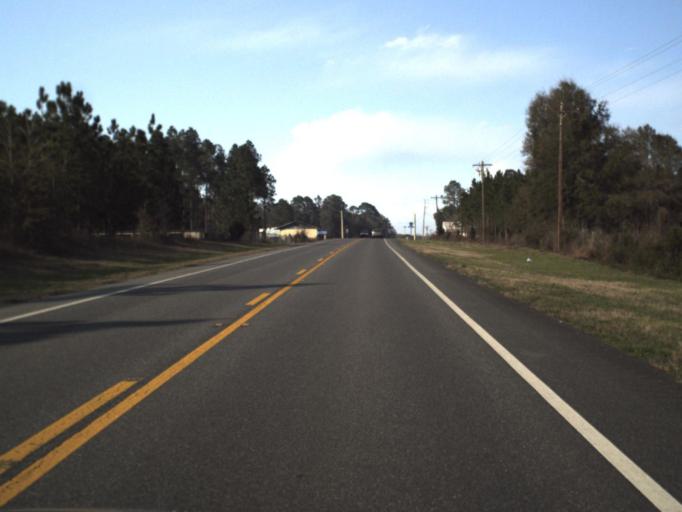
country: US
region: Florida
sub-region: Calhoun County
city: Blountstown
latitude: 30.5324
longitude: -85.1926
